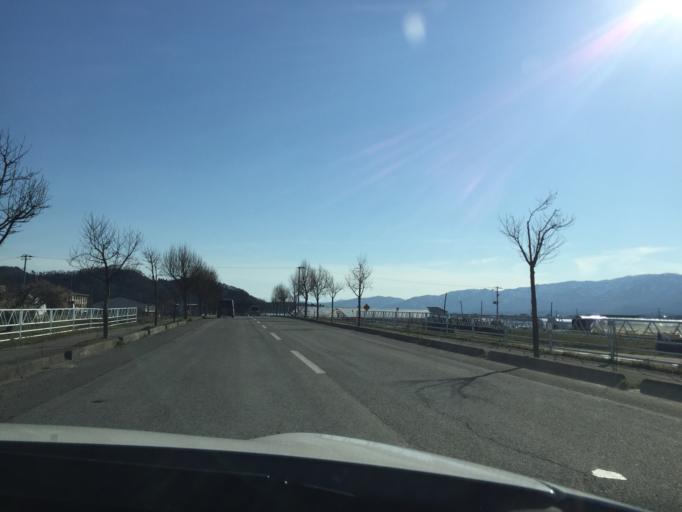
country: JP
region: Yamagata
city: Nagai
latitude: 38.1676
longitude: 140.0862
